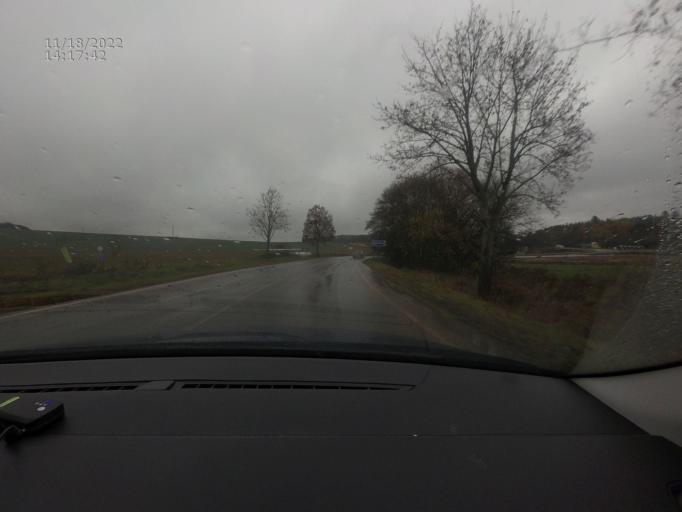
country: CZ
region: Jihocesky
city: Mirotice
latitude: 49.4377
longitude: 14.0493
